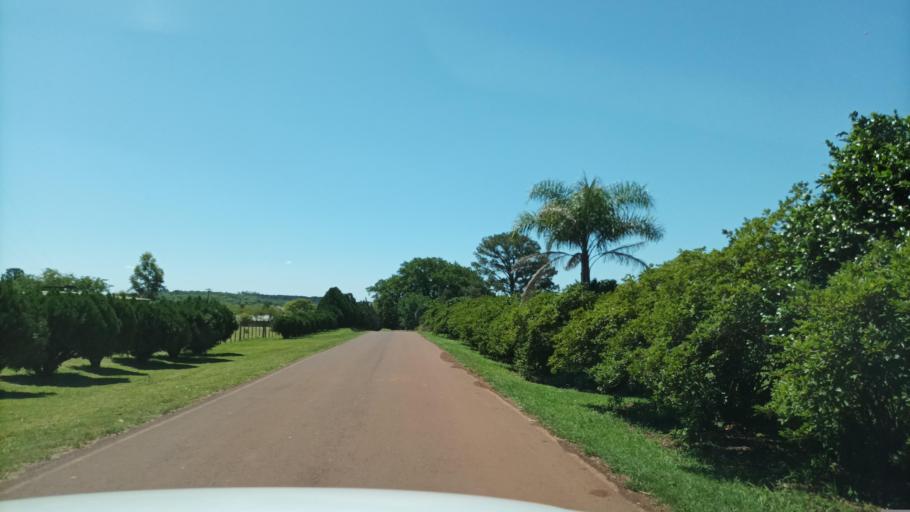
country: AR
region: Misiones
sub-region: Departamento de Apostoles
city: San Jose
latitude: -27.7913
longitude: -55.7157
